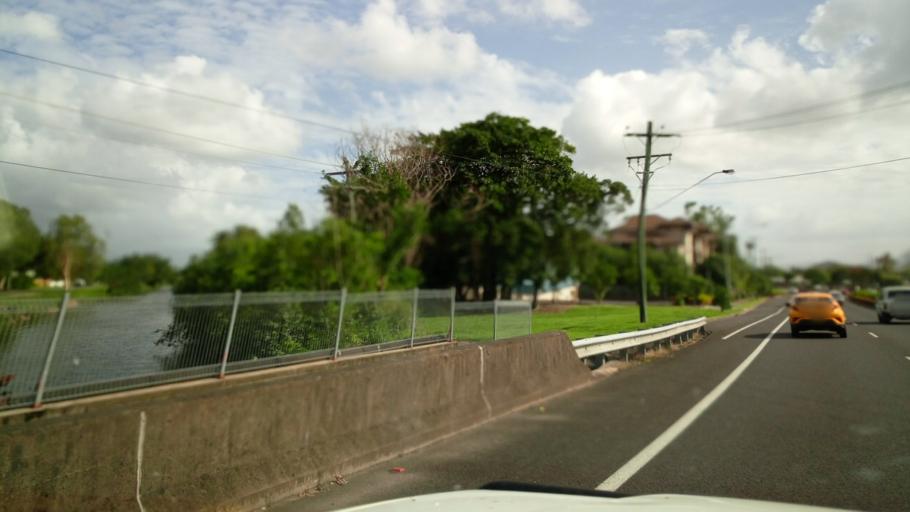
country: AU
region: Queensland
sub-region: Cairns
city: Woree
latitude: -16.9317
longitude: 145.7434
